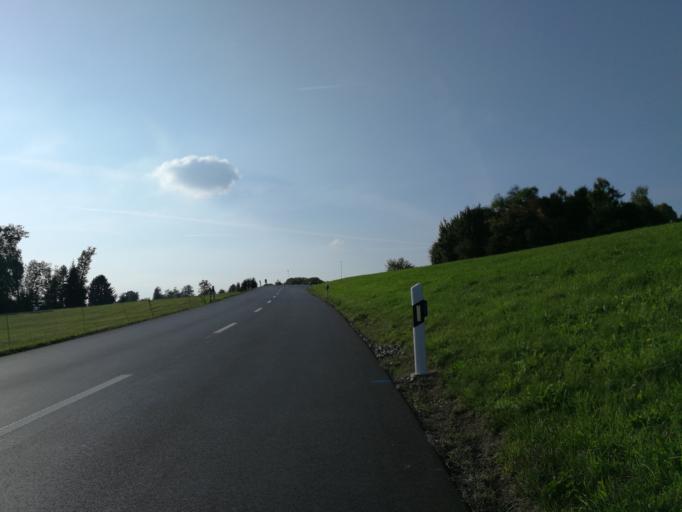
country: CH
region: Zurich
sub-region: Bezirk Meilen
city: Stafa
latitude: 47.2534
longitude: 8.7235
